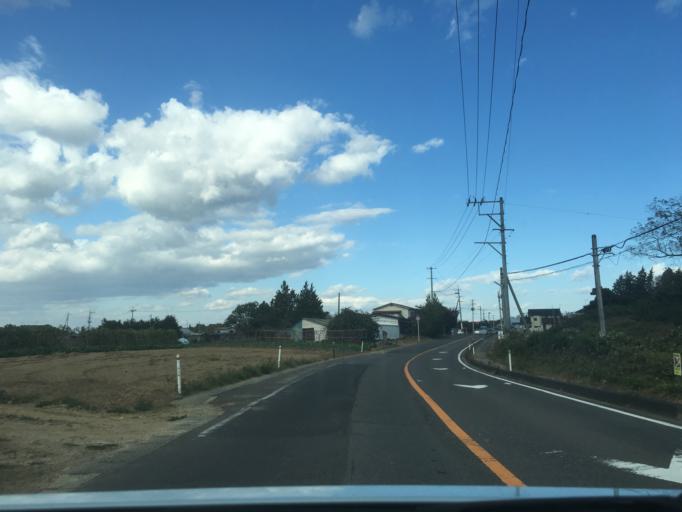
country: JP
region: Fukushima
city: Sukagawa
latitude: 37.3078
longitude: 140.4076
